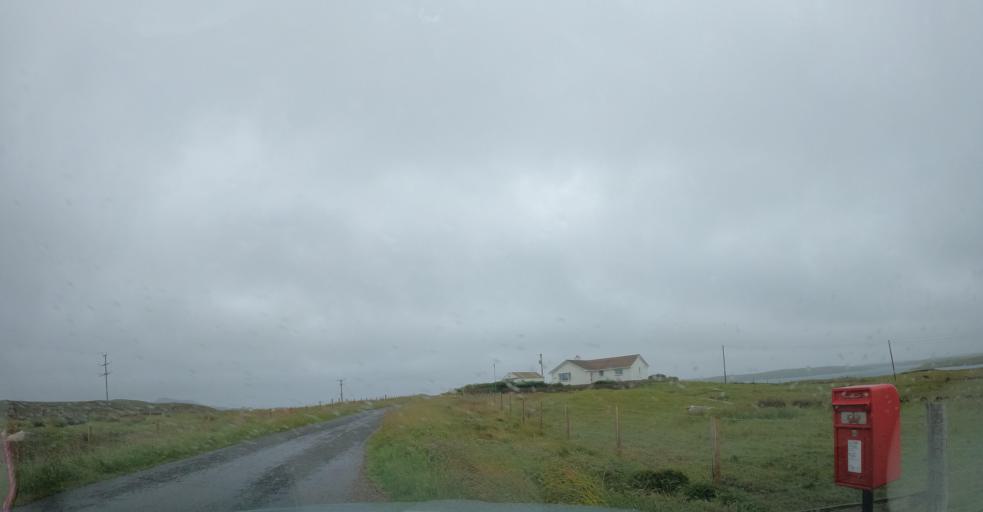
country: GB
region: Scotland
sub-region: Eilean Siar
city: Benbecula
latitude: 57.4812
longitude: -7.2271
